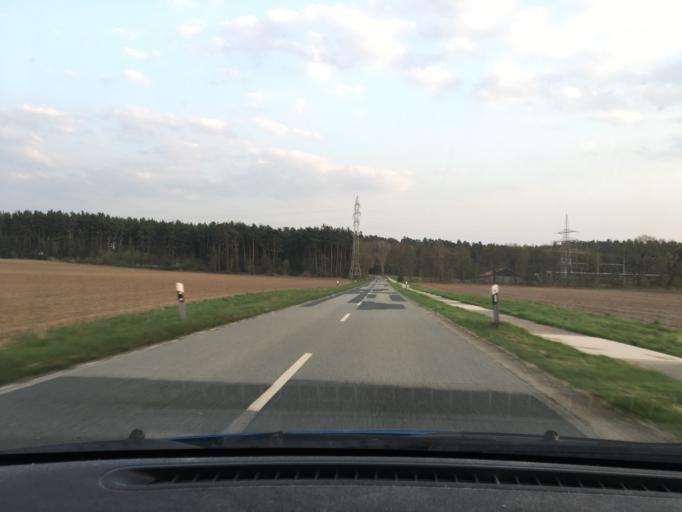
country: DE
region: Lower Saxony
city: Oldendorf
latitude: 53.1696
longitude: 10.2455
